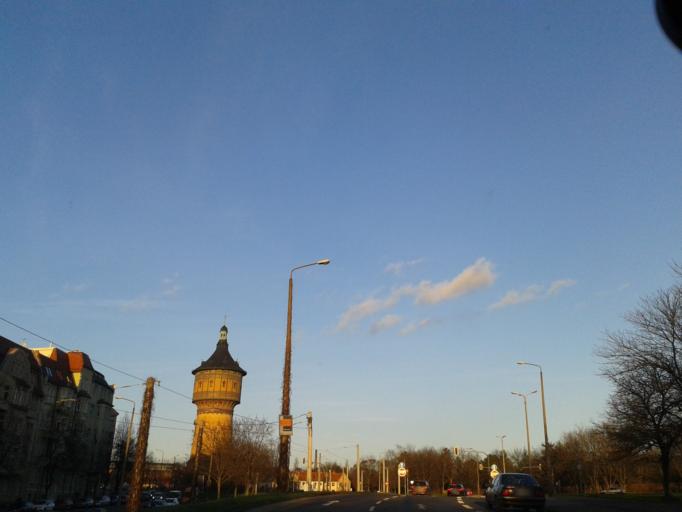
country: DE
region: Saxony-Anhalt
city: Halle (Saale)
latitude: 51.4909
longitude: 11.9803
